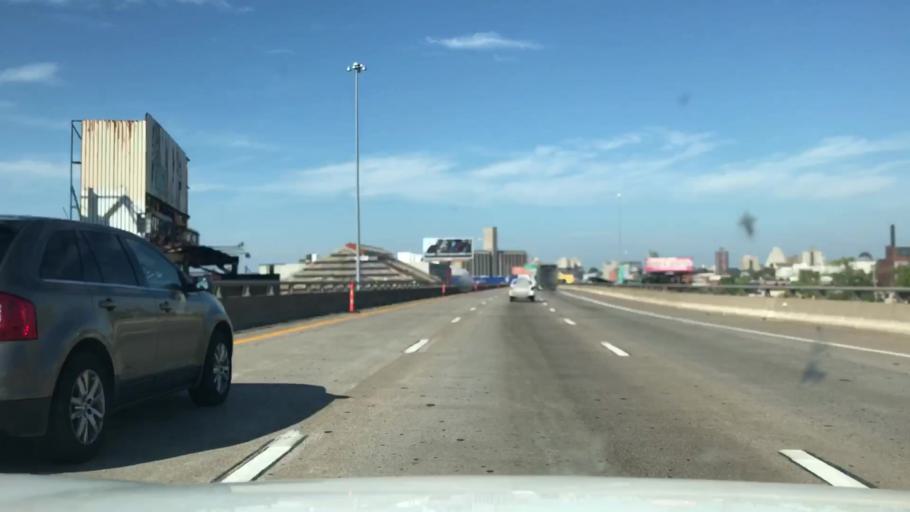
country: US
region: Missouri
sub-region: City of Saint Louis
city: St. Louis
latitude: 38.6314
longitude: -90.2341
